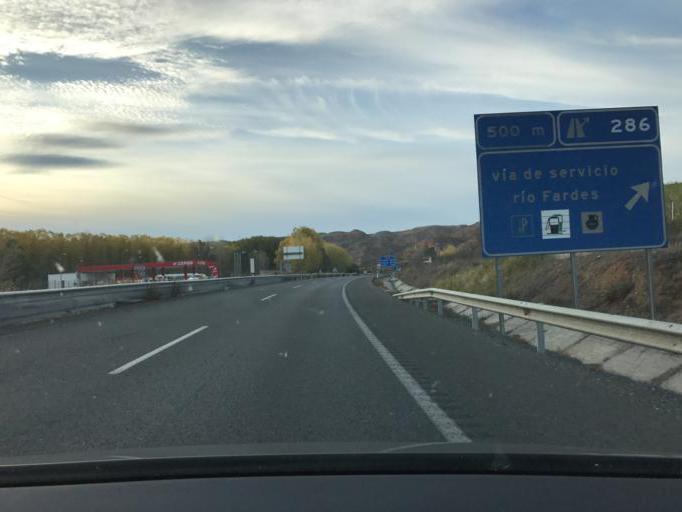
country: ES
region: Andalusia
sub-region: Provincia de Granada
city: Purullena
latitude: 37.3288
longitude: -3.2149
